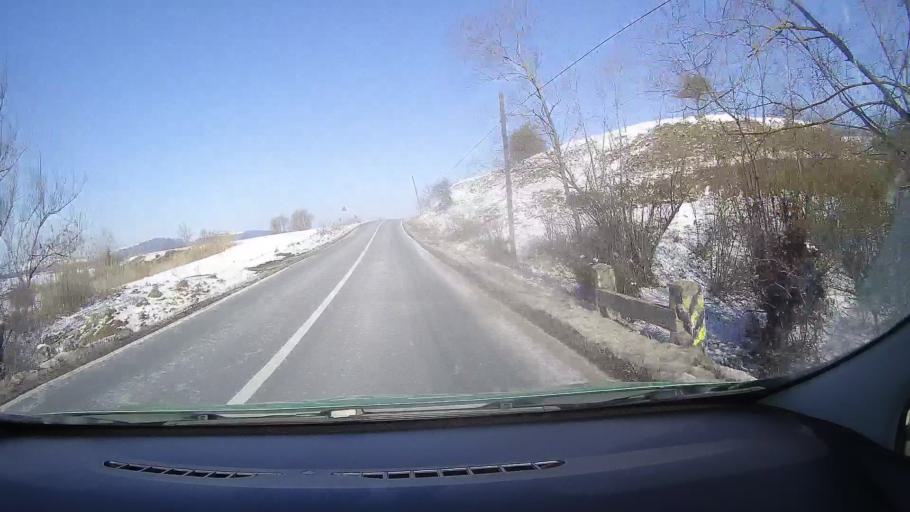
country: RO
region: Brasov
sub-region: Comuna Comana
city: Comana de Jos
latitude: 45.9014
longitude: 25.2270
